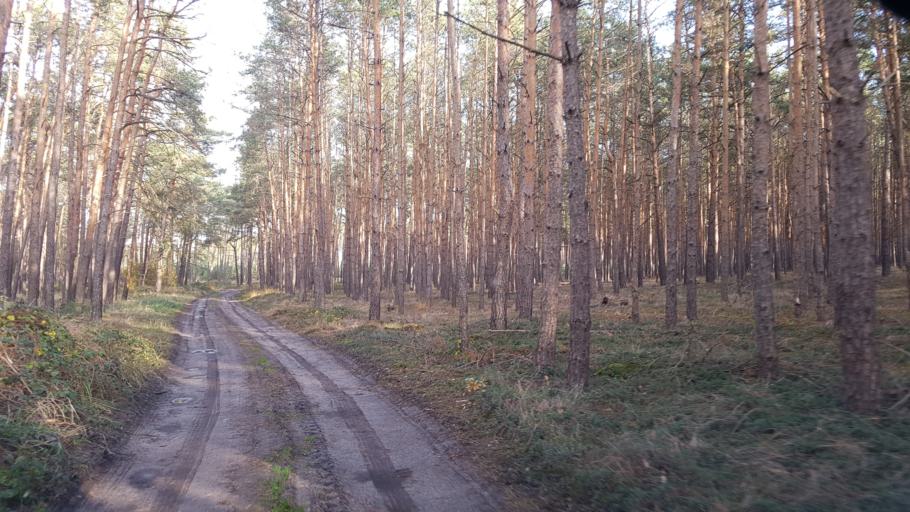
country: DE
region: Brandenburg
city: Trobitz
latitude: 51.6524
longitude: 13.4232
